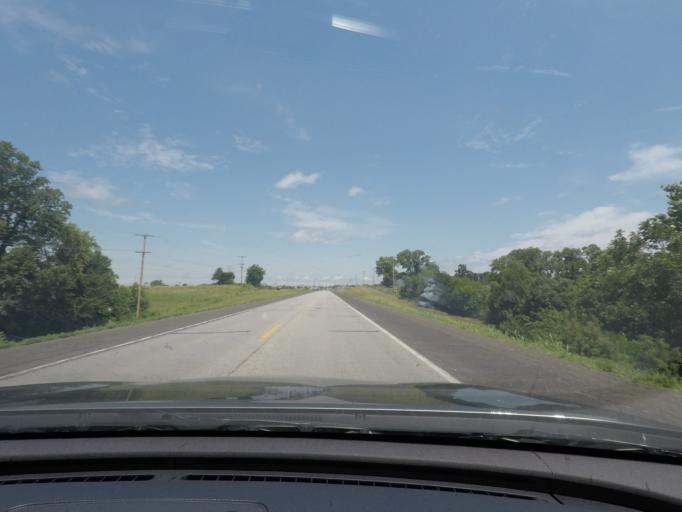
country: US
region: Missouri
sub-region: Saline County
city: Marshall
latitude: 39.0990
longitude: -93.2136
